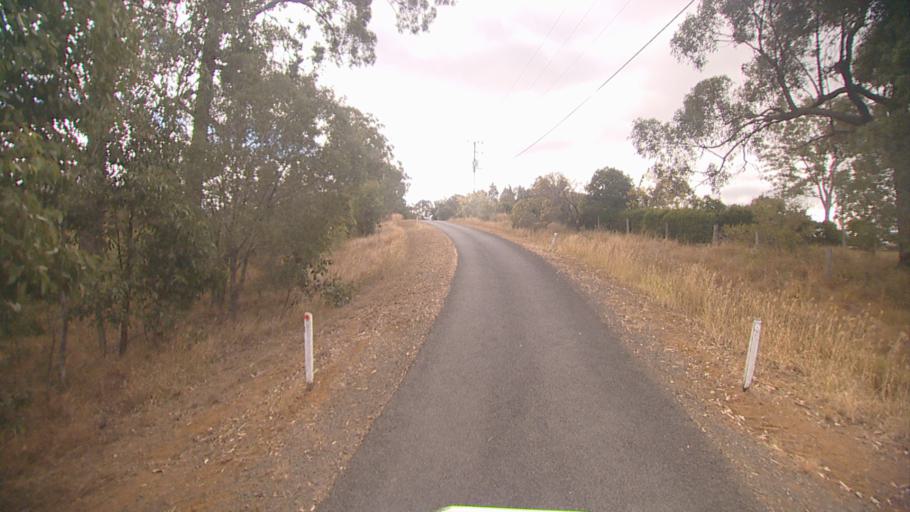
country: AU
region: Queensland
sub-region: Logan
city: Cedar Vale
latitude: -27.9013
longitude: 153.0383
